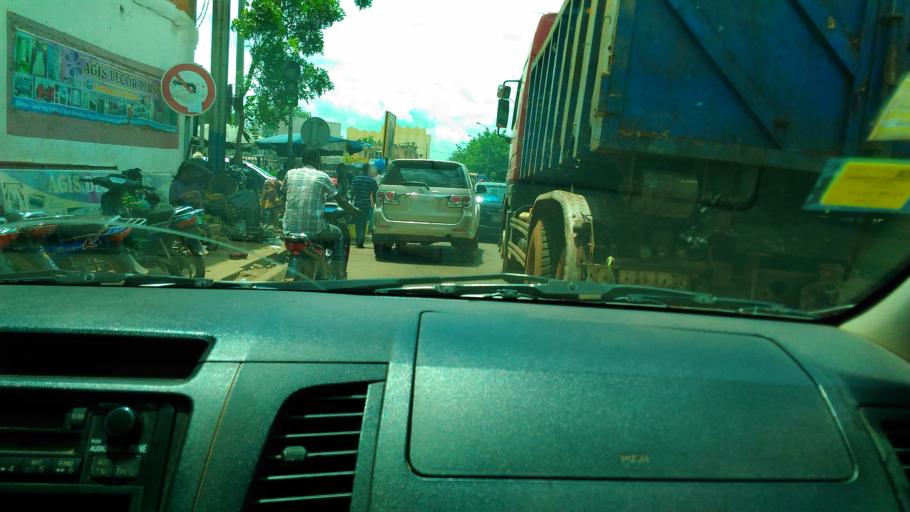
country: ML
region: Bamako
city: Bamako
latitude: 12.6511
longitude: -7.9939
